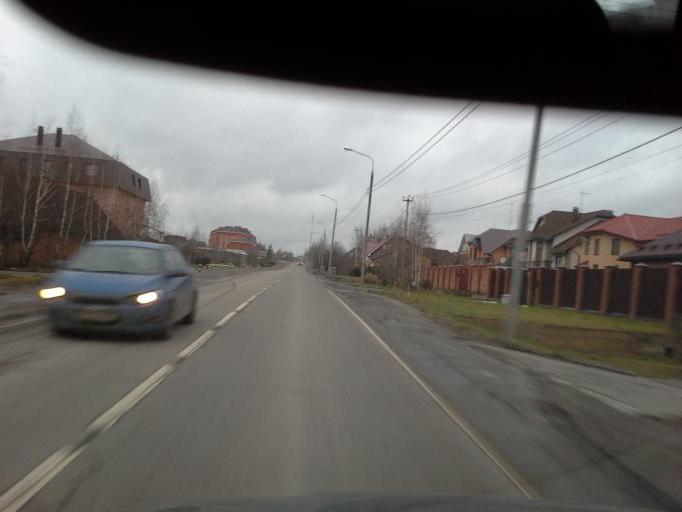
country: RU
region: Moscow
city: Vnukovo
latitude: 55.5993
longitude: 37.2013
